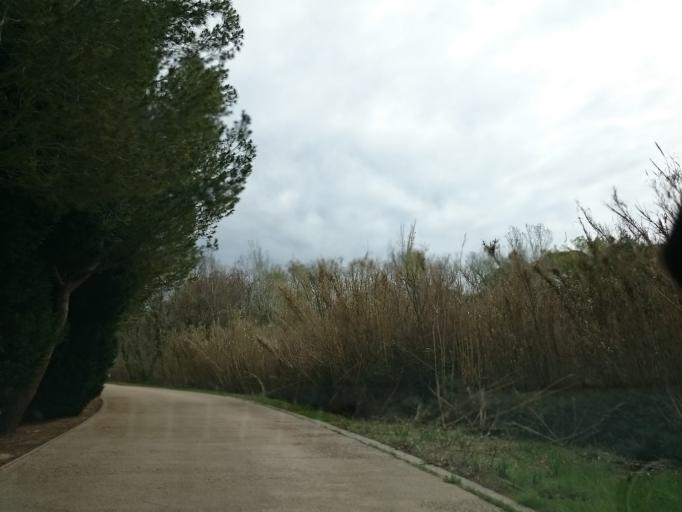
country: ES
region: Catalonia
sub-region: Provincia de Barcelona
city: Sant Sadurni d'Anoia
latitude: 41.4286
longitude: 1.8024
